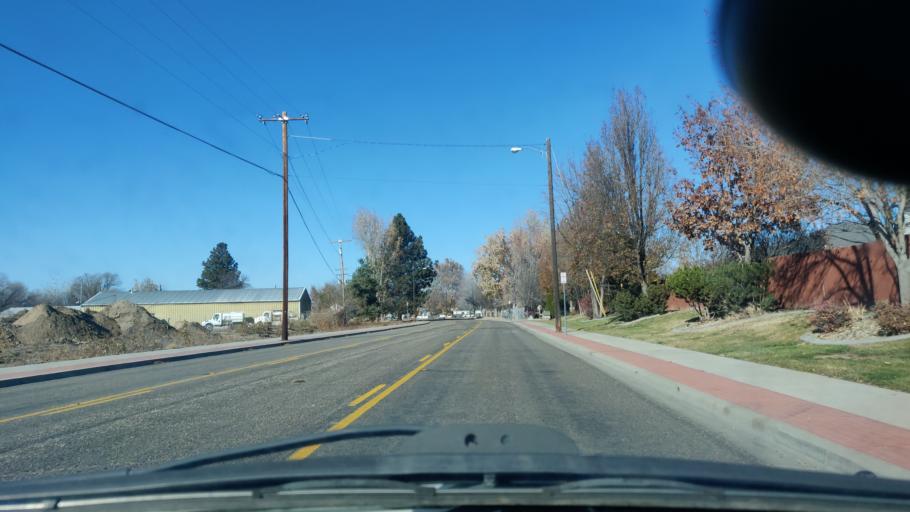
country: US
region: Idaho
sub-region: Ada County
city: Garden City
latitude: 43.6435
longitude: -116.2597
